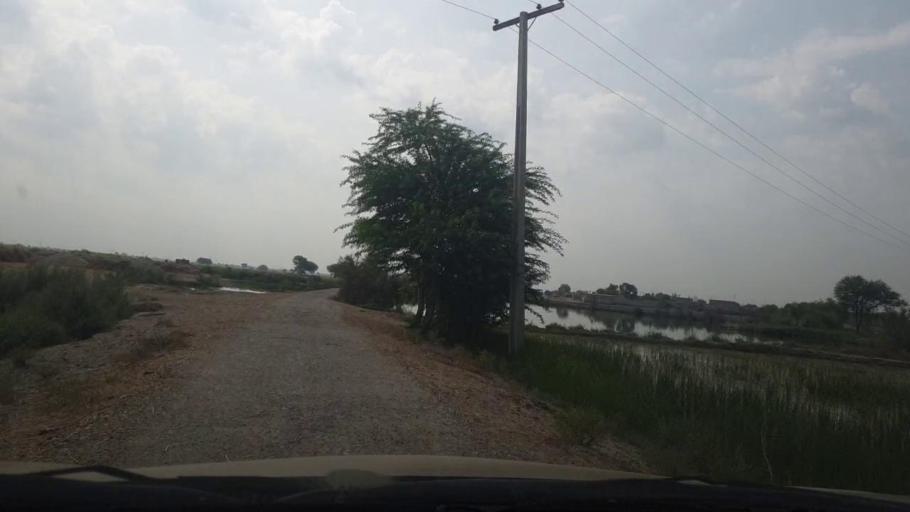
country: PK
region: Sindh
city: Larkana
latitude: 27.6521
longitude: 68.2089
